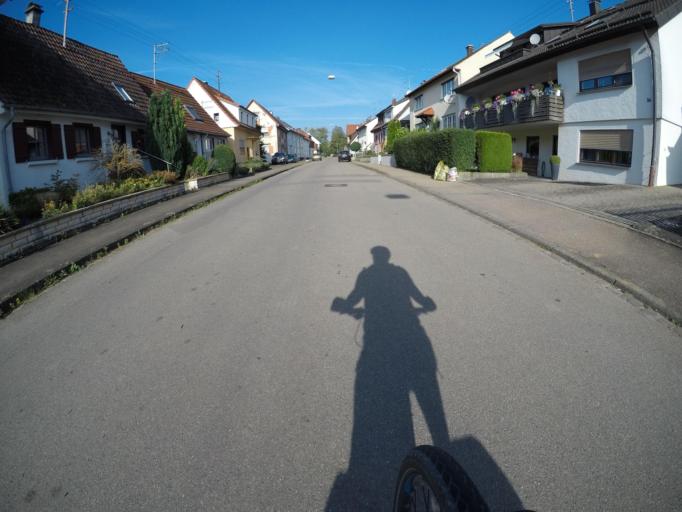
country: DE
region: Baden-Wuerttemberg
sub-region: Regierungsbezirk Stuttgart
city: Bolheim
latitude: 48.5999
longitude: 10.1218
